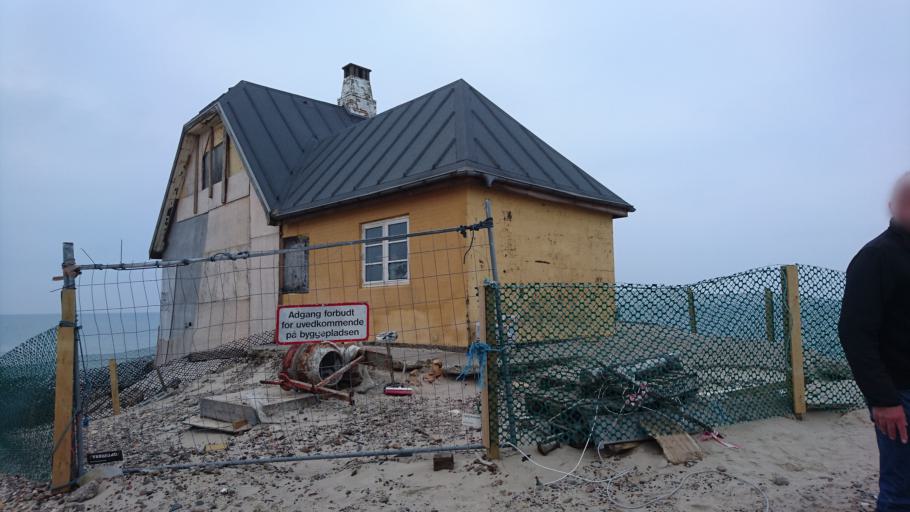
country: DK
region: North Denmark
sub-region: Frederikshavn Kommune
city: Skagen
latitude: 57.7243
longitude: 10.5125
